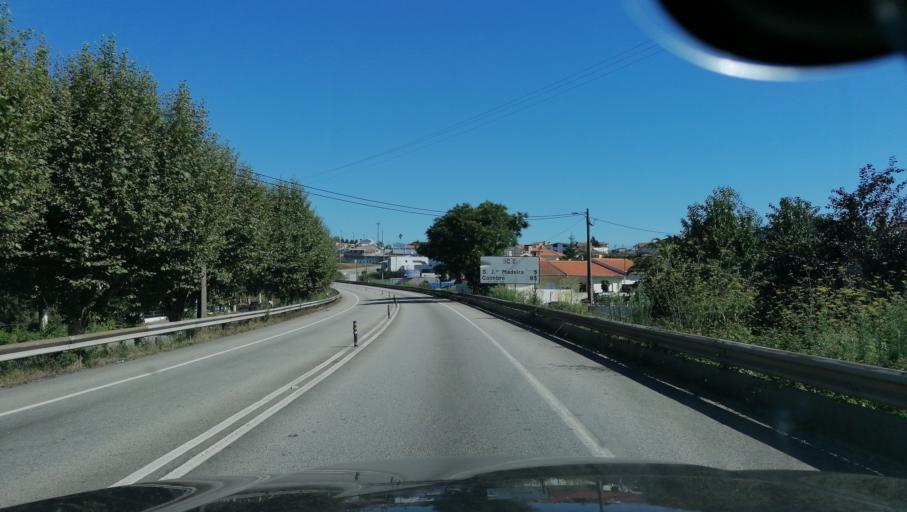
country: PT
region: Aveiro
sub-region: Santa Maria da Feira
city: Arrifana
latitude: 40.9215
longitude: -8.5009
